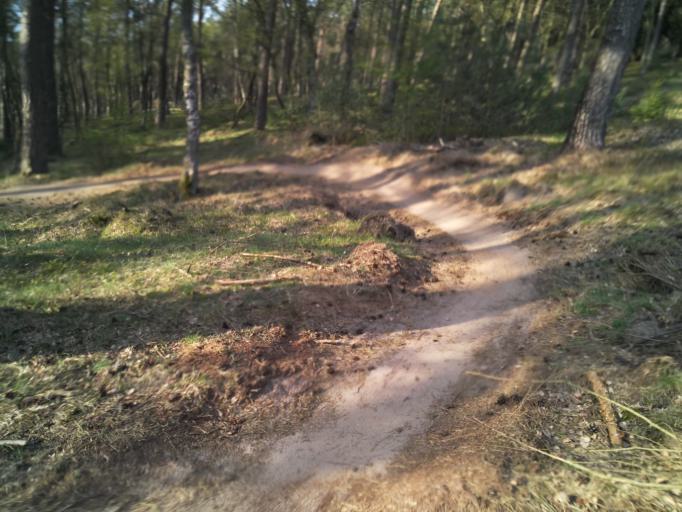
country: NL
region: Gelderland
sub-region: Gemeente Renkum
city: Wolfheze
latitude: 52.0374
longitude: 5.7546
